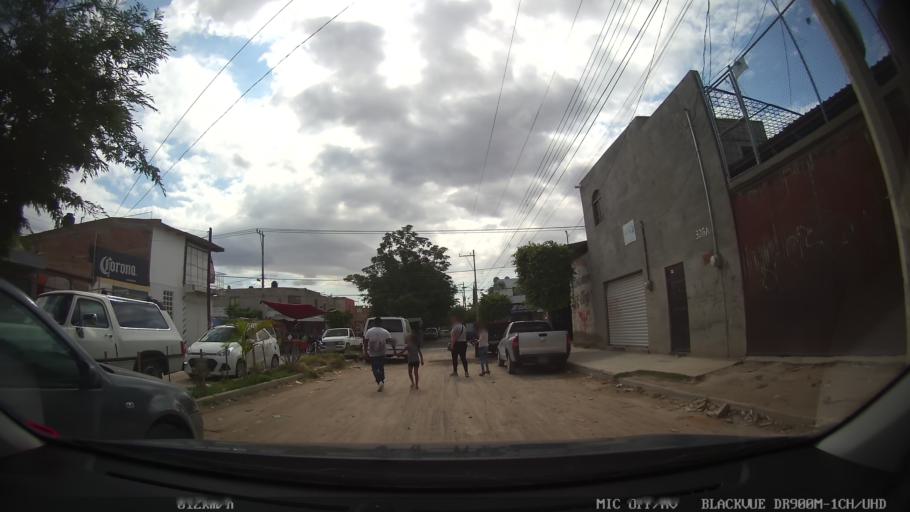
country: MX
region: Jalisco
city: Tlaquepaque
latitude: 20.6699
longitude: -103.2541
